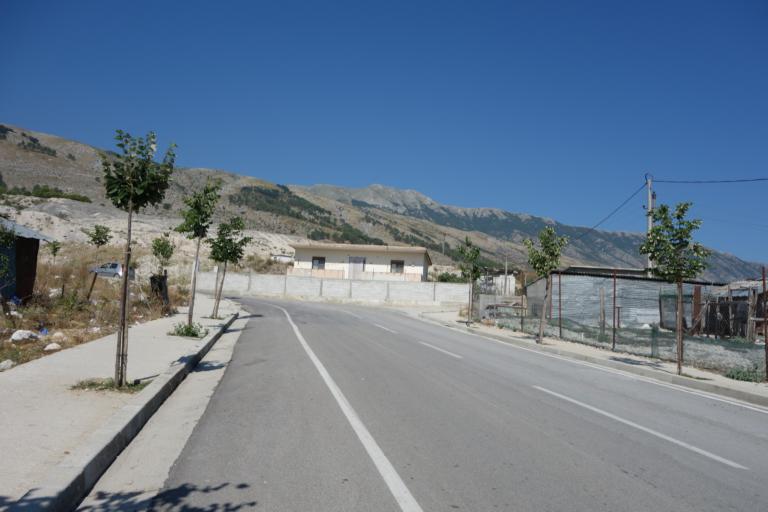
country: AL
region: Gjirokaster
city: Gjirokaster
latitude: 40.0860
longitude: 20.1319
